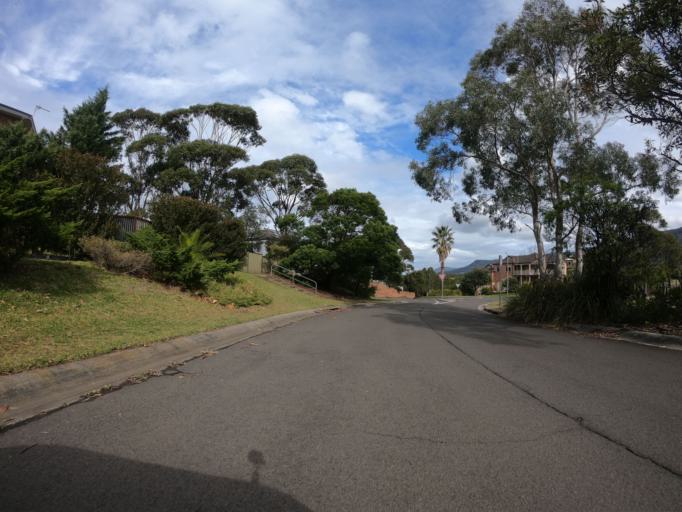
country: AU
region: New South Wales
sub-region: Wollongong
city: Bulli
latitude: -34.3214
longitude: 150.9226
